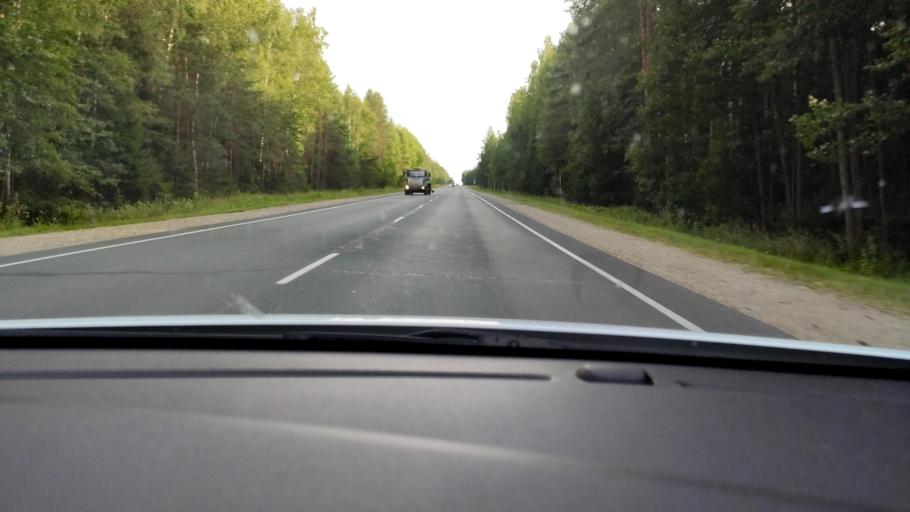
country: RU
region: Mariy-El
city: Suslonger
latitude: 56.2653
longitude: 48.2328
